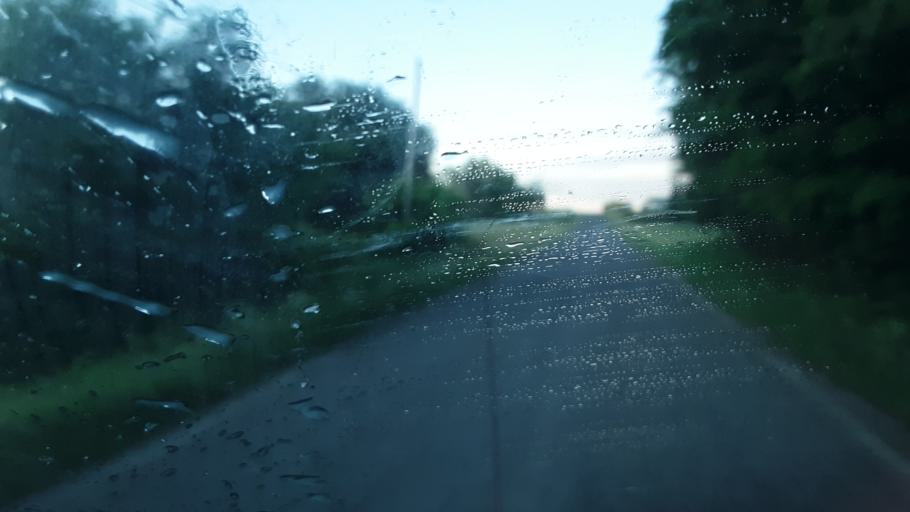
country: US
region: Maine
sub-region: Aroostook County
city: Caribou
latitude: 46.8243
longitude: -68.1356
